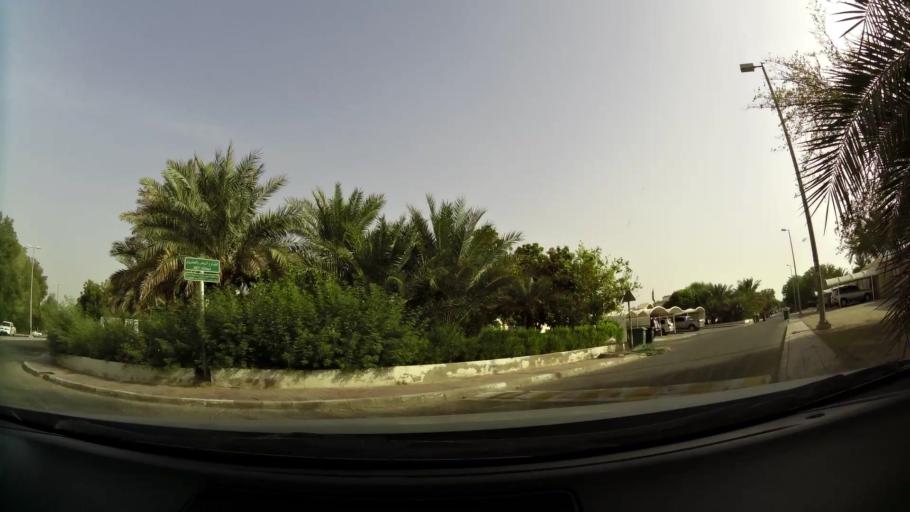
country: AE
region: Abu Dhabi
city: Al Ain
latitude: 24.1364
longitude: 55.6870
